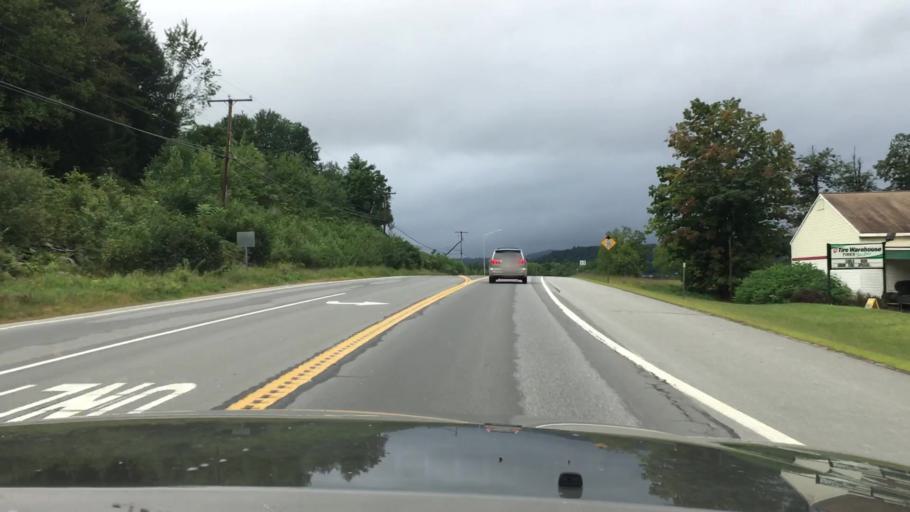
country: US
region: Vermont
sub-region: Windham County
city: Brattleboro
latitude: 42.8857
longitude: -72.5386
